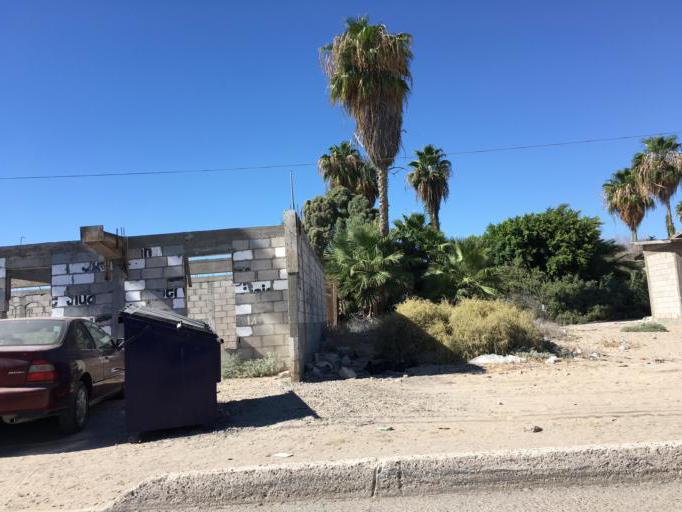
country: MX
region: Sonora
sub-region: Puerto Penasco
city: Puerto Penasco
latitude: 31.3121
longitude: -113.5332
